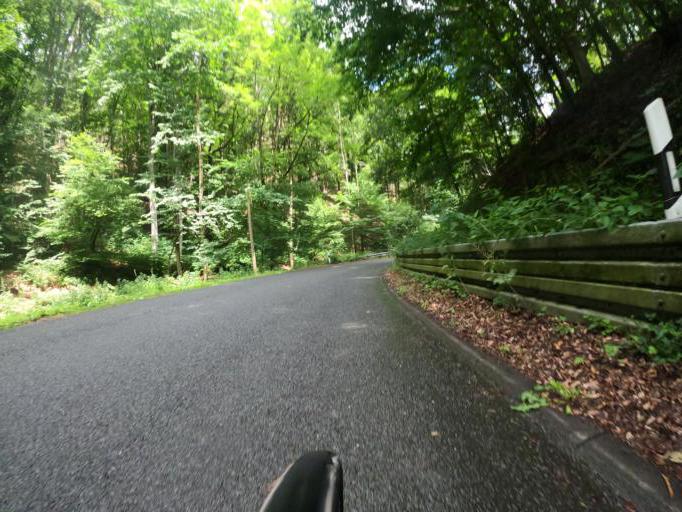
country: DE
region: Hesse
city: Witzenhausen
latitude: 51.3053
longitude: 9.8723
